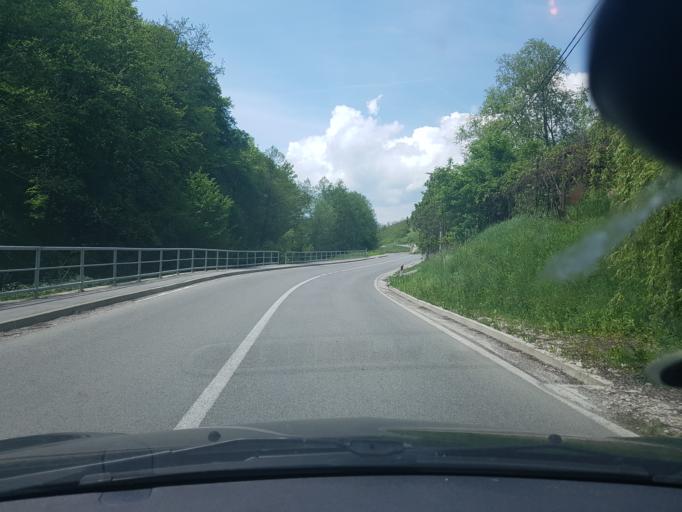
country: HR
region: Krapinsko-Zagorska
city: Pregrada
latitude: 46.1898
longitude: 15.7315
